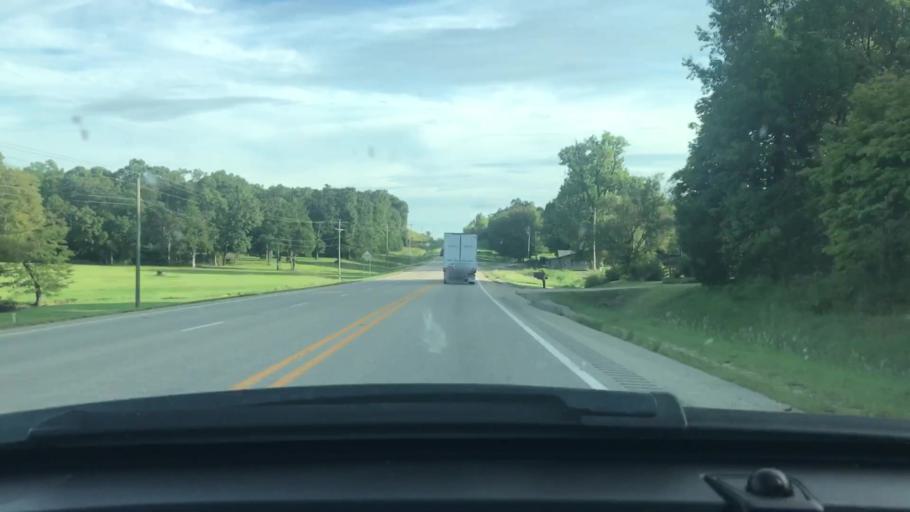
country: US
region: Arkansas
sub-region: Lawrence County
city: Hoxie
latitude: 36.1529
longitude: -91.1611
